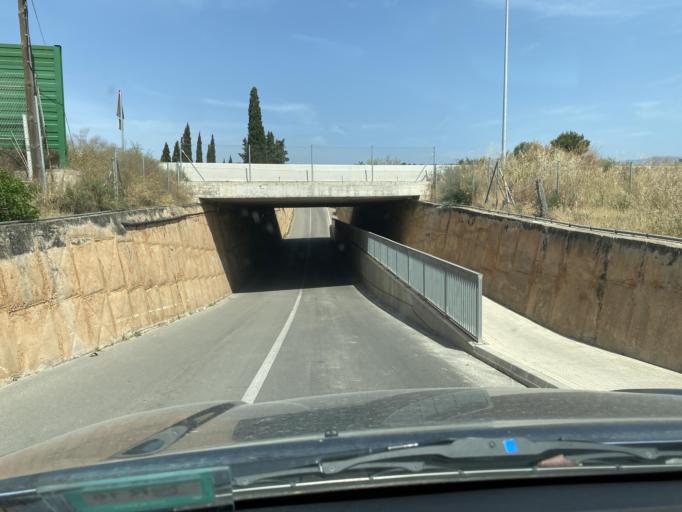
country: ES
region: Balearic Islands
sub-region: Illes Balears
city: Marratxi
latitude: 39.6225
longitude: 2.7117
